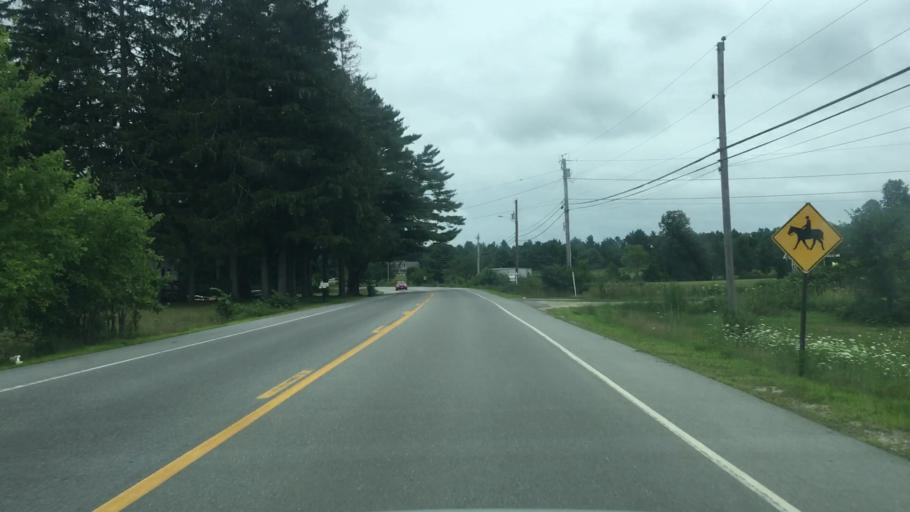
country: US
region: Maine
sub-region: York County
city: Biddeford
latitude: 43.5185
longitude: -70.4813
